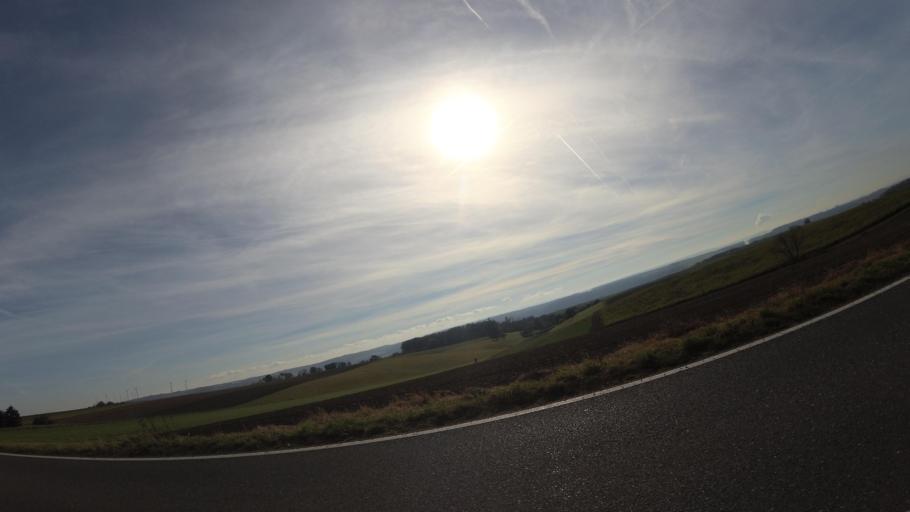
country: DE
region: Baden-Wuerttemberg
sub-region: Regierungsbezirk Stuttgart
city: Mockmuhl
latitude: 49.3202
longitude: 9.3205
